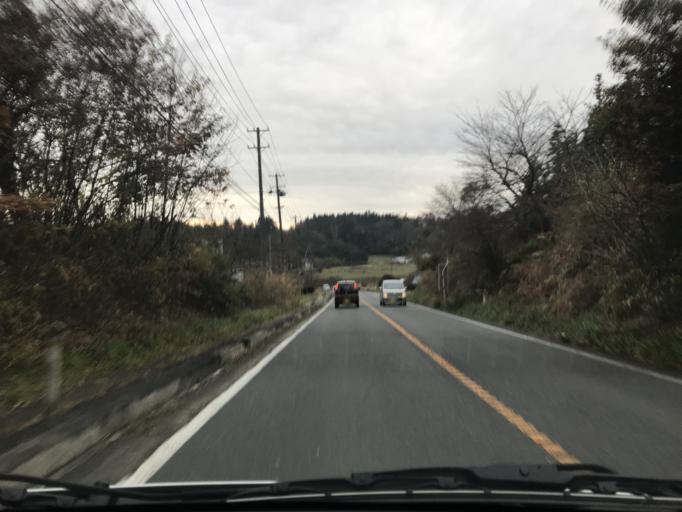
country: JP
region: Iwate
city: Ichinoseki
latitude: 39.0100
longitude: 141.3272
